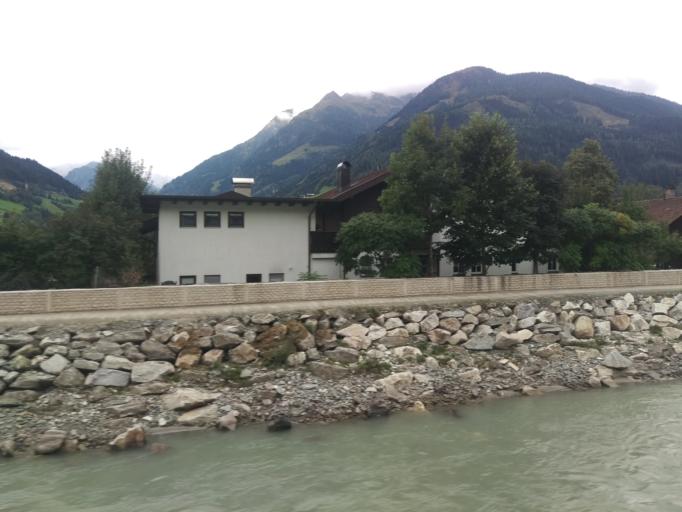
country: AT
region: Salzburg
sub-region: Politischer Bezirk Zell am See
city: Mittersill
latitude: 47.2837
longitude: 12.4851
